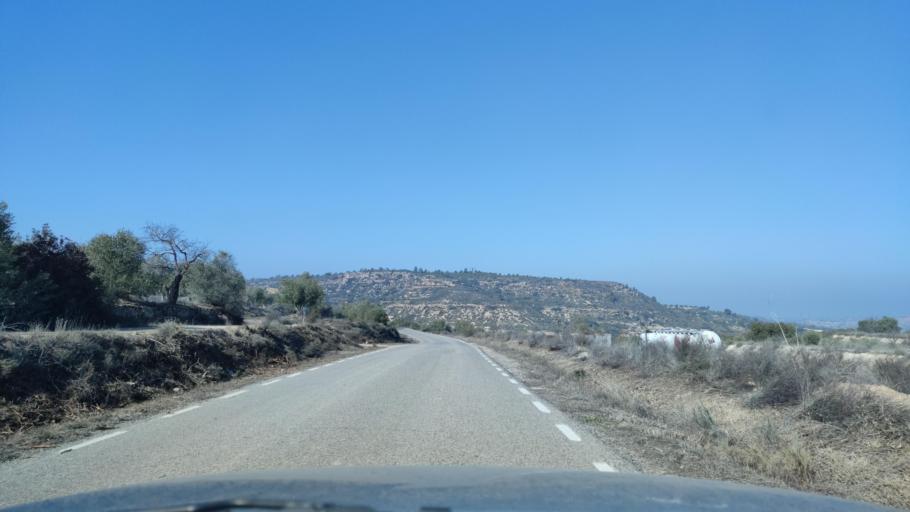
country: ES
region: Catalonia
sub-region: Provincia de Lleida
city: Torrebesses
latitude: 41.4291
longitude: 0.5844
